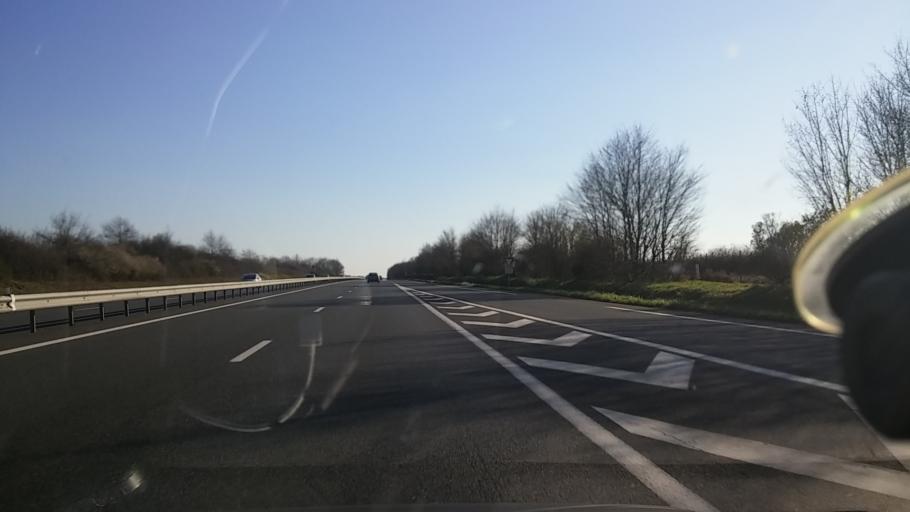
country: FR
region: Centre
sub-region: Departement de l'Indre
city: Chantome
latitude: 46.4414
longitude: 1.4824
